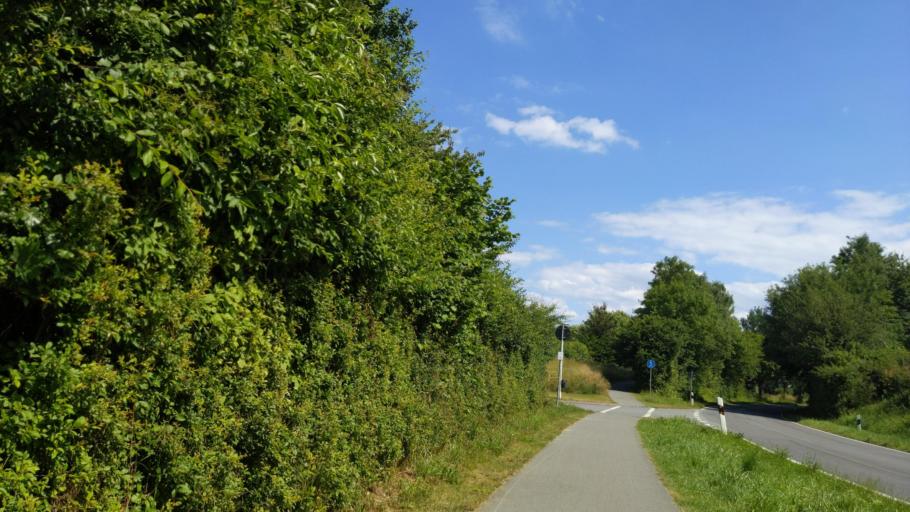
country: DE
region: Schleswig-Holstein
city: Gromitz
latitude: 54.1530
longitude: 10.9453
